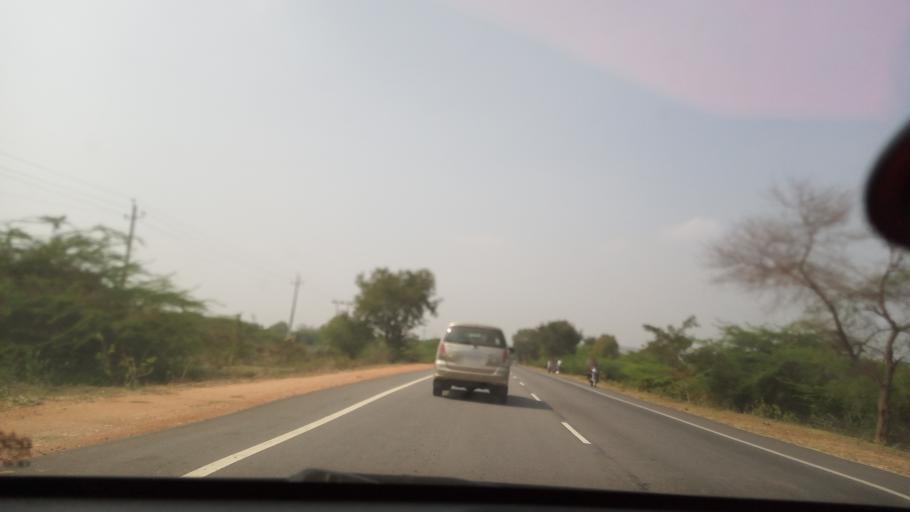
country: IN
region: Karnataka
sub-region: Mysore
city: Nanjangud
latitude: 12.0748
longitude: 76.7407
